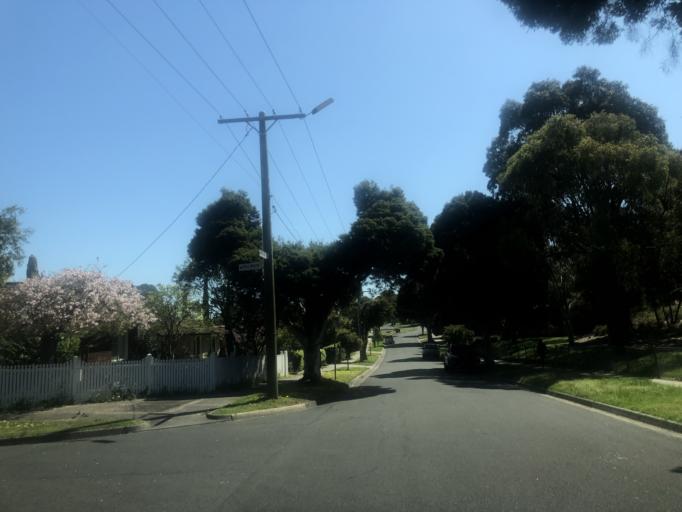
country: AU
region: Victoria
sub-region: Monash
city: Notting Hill
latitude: -37.9037
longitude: 145.1724
